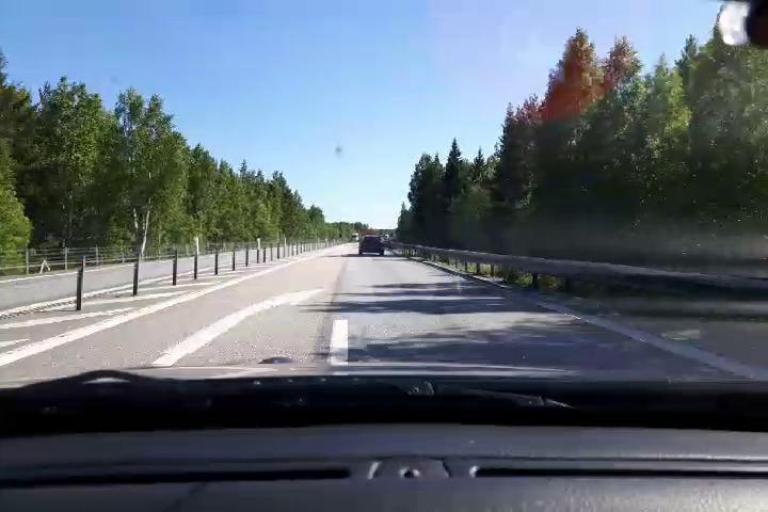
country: SE
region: Gaevleborg
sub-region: Gavle Kommun
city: Norrsundet
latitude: 60.9199
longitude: 17.0128
